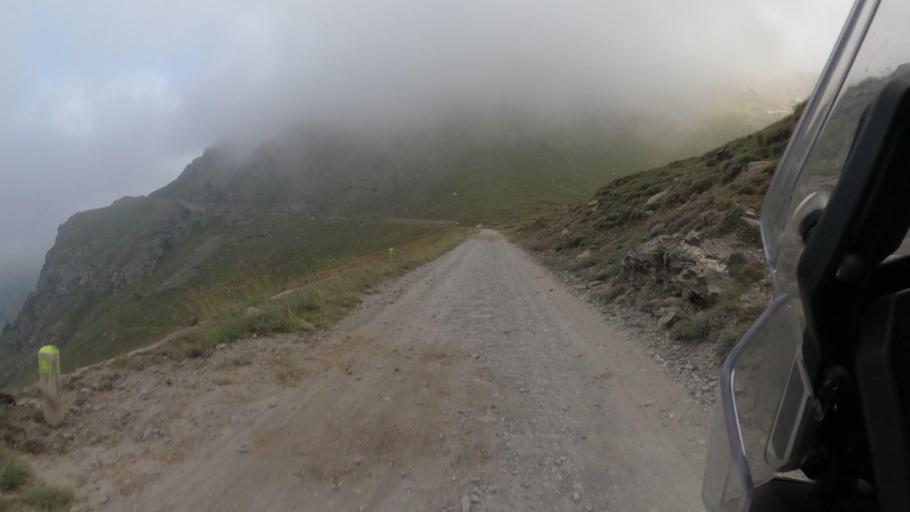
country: IT
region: Piedmont
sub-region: Provincia di Torino
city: Usseaux
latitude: 45.0625
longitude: 6.9753
